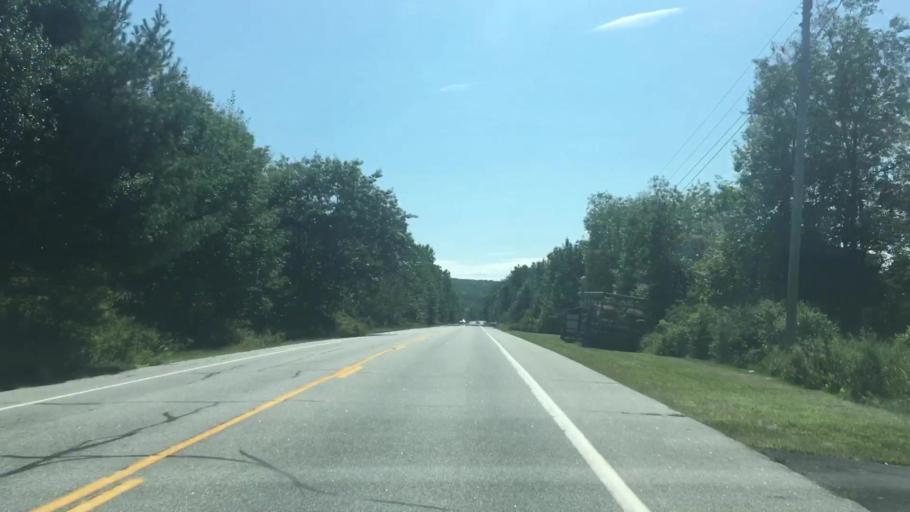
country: US
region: Maine
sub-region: Androscoggin County
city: Sabattus
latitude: 44.1564
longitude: -70.0348
